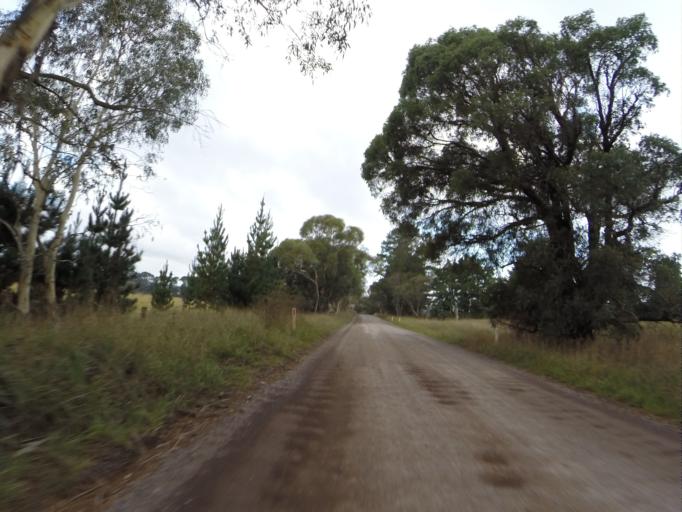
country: AU
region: New South Wales
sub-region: Wingecarribee
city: Moss Vale
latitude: -34.5330
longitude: 150.2748
